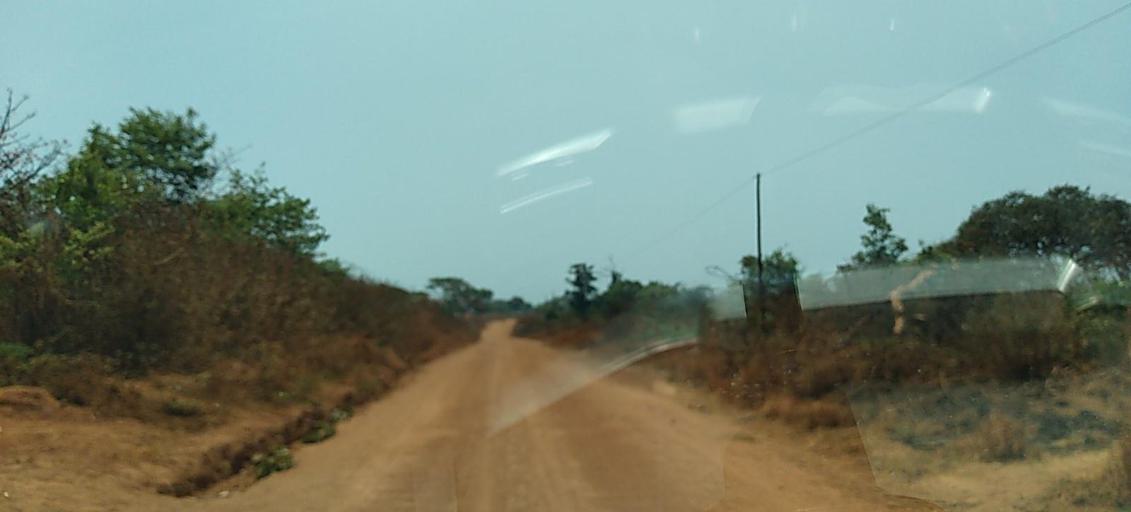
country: CD
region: Katanga
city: Kipushi
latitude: -11.9371
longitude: 26.9566
